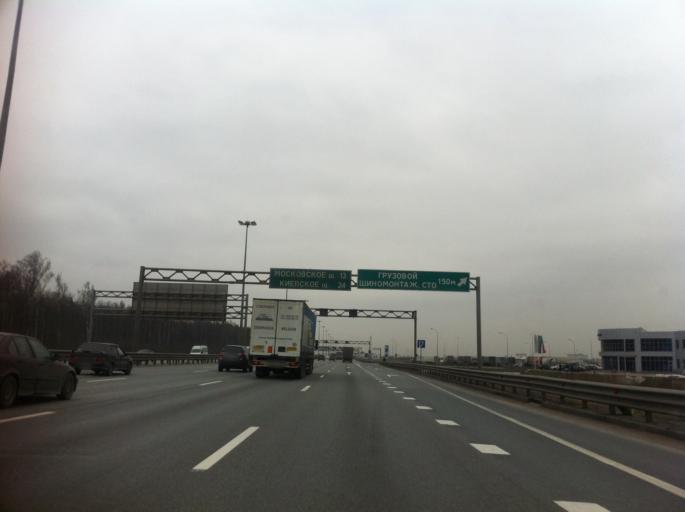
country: RU
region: Leningrad
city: Rybatskoye
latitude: 59.8819
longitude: 30.5271
